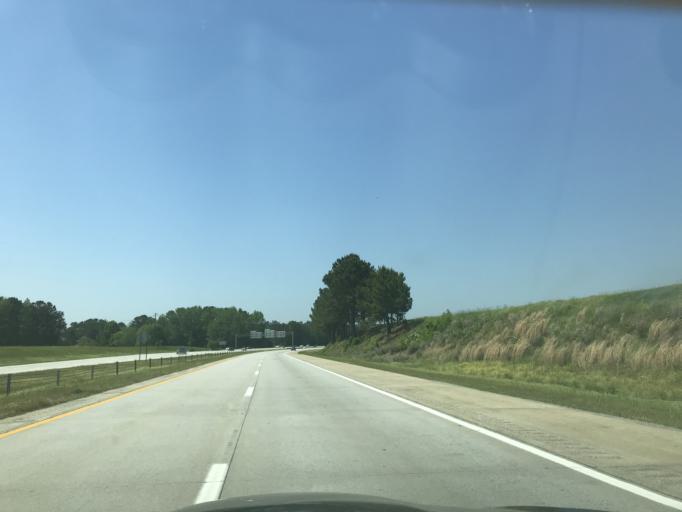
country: US
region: North Carolina
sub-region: Johnston County
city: Benson
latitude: 35.3918
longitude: -78.5195
